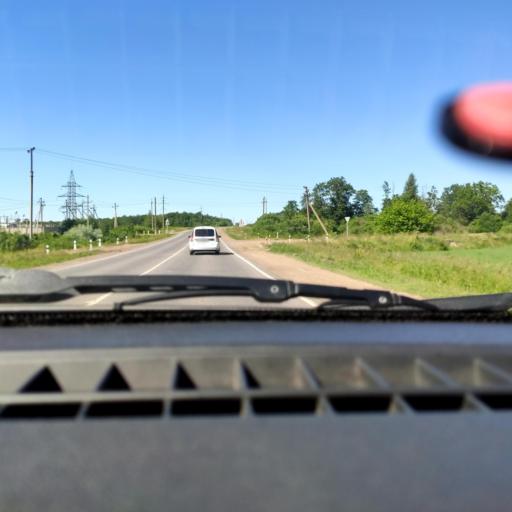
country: RU
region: Bashkortostan
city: Iglino
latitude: 54.8808
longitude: 56.4698
